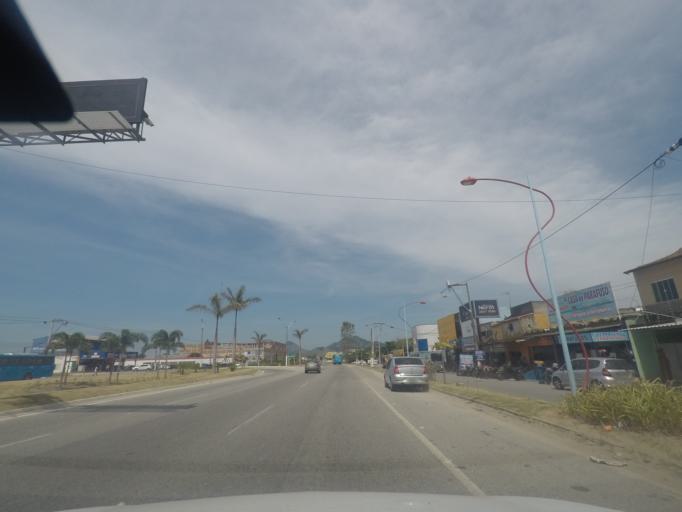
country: BR
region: Rio de Janeiro
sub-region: Marica
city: Marica
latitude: -22.9075
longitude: -42.8254
